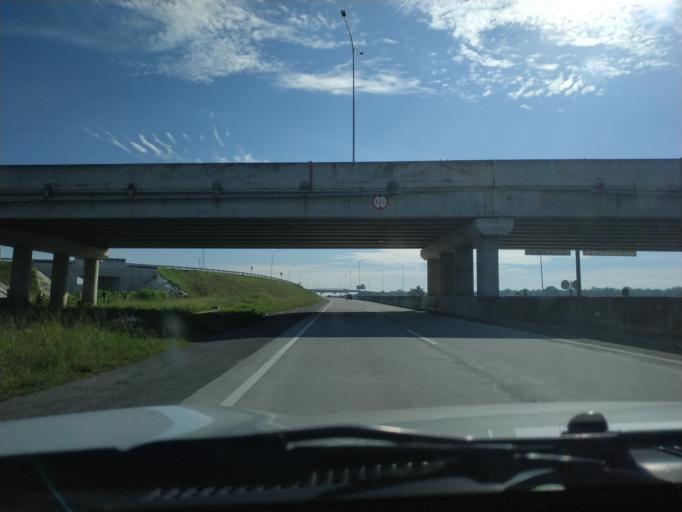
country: ID
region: North Sumatra
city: Perbaungan
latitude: 3.5328
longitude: 98.8933
